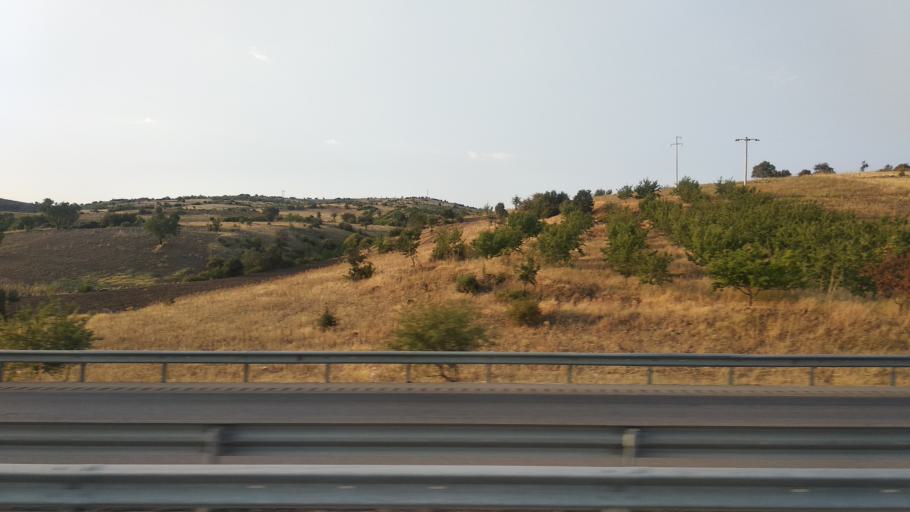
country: TR
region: Manisa
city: Menye
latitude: 38.5675
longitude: 28.5692
